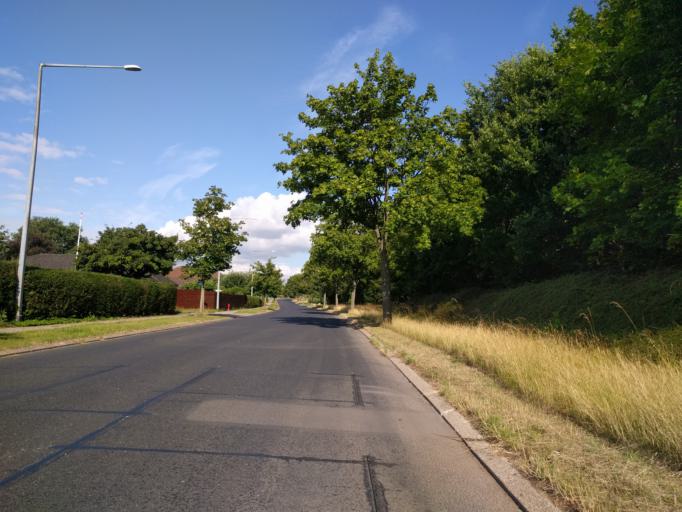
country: DK
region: South Denmark
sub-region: Kerteminde Kommune
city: Kerteminde
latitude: 55.4572
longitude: 10.6467
